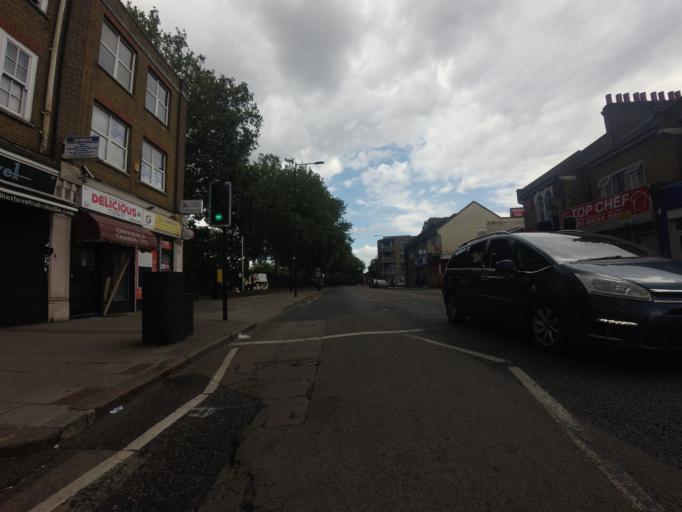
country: GB
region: England
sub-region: Greater London
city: Poplar
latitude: 51.5391
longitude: 0.0047
